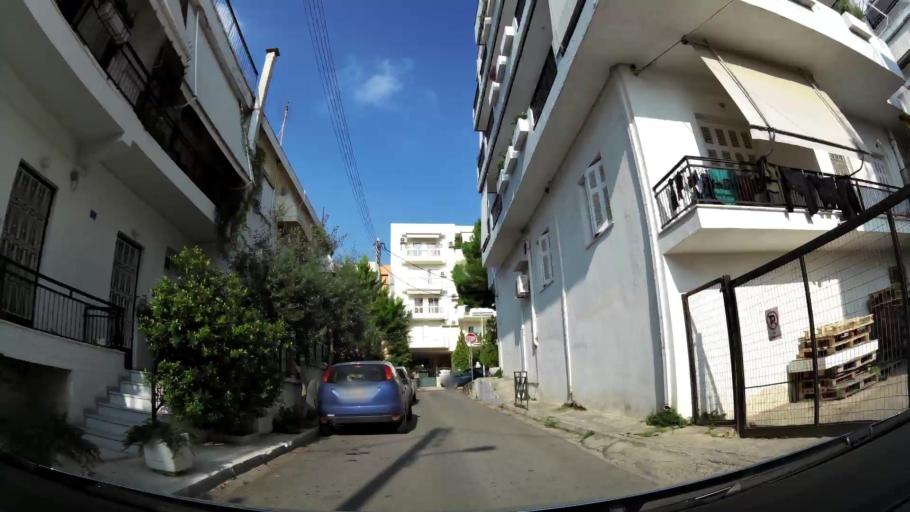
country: GR
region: Attica
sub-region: Nomarchia Athinas
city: Cholargos
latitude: 38.0000
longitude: 23.8156
